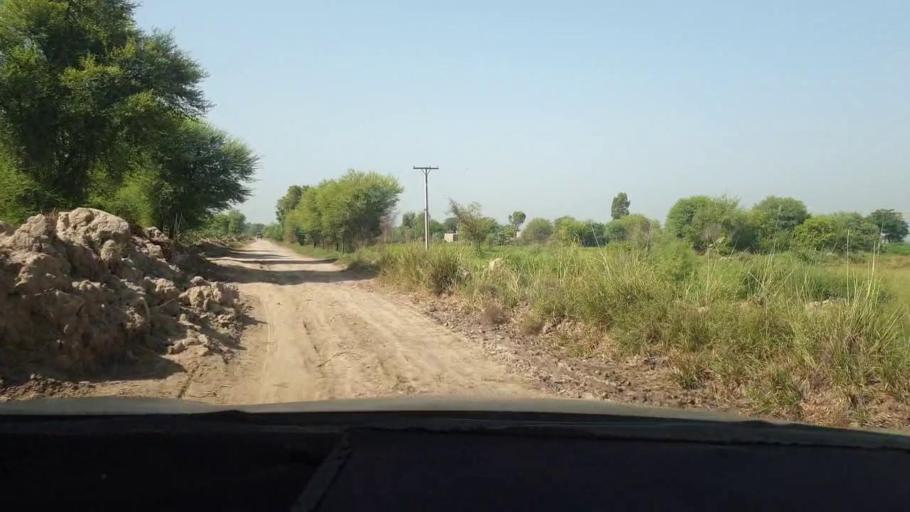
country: PK
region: Sindh
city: Miro Khan
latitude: 27.7201
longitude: 68.1127
